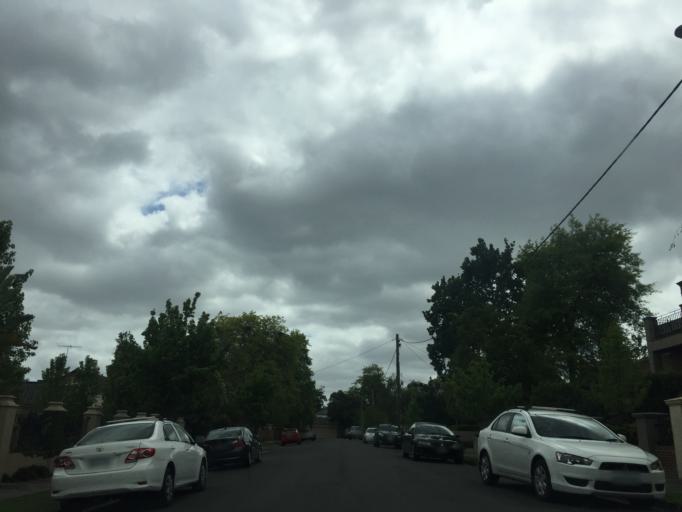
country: AU
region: Victoria
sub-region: Boroondara
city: Kew East
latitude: -37.8050
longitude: 145.0519
